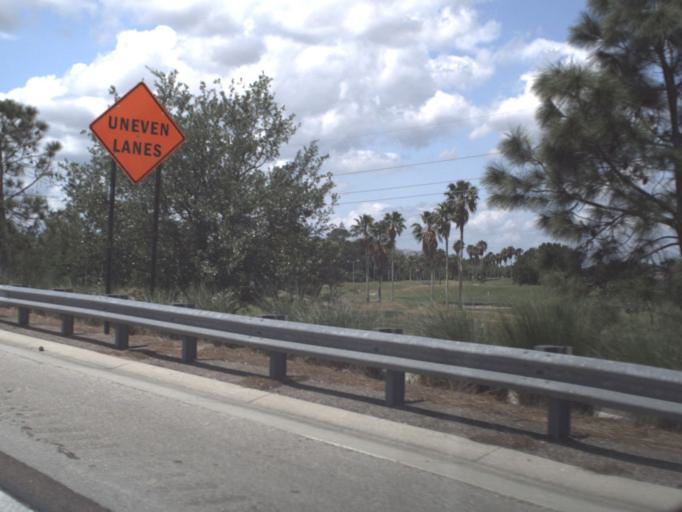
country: US
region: Florida
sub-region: Orange County
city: Oakland
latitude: 28.5128
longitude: -81.6043
